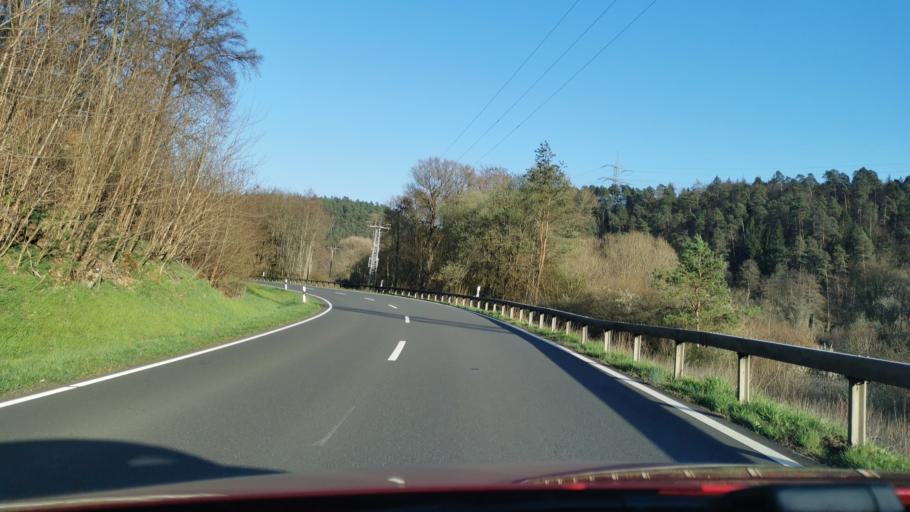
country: DE
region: Rheinland-Pfalz
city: Kordel
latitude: 49.8231
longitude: 6.6519
